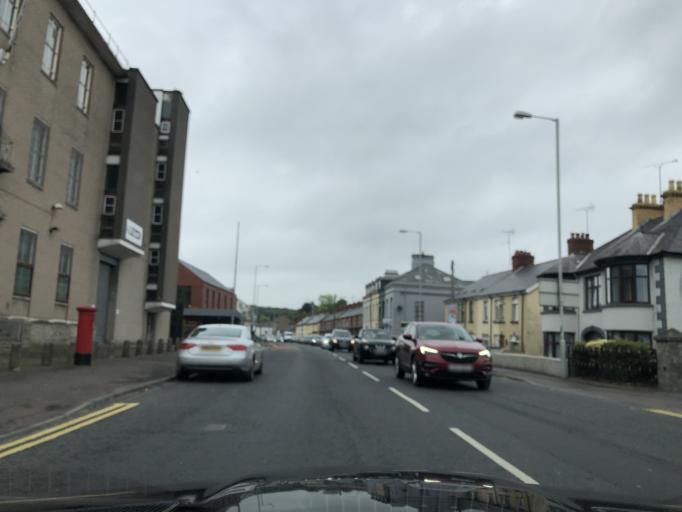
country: GB
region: Northern Ireland
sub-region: Down District
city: Downpatrick
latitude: 54.3313
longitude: -5.7155
